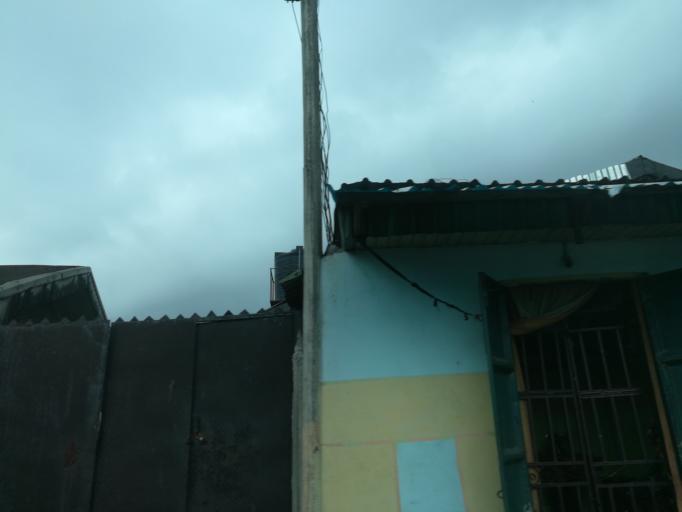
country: NG
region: Rivers
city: Port Harcourt
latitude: 4.8211
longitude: 7.0180
